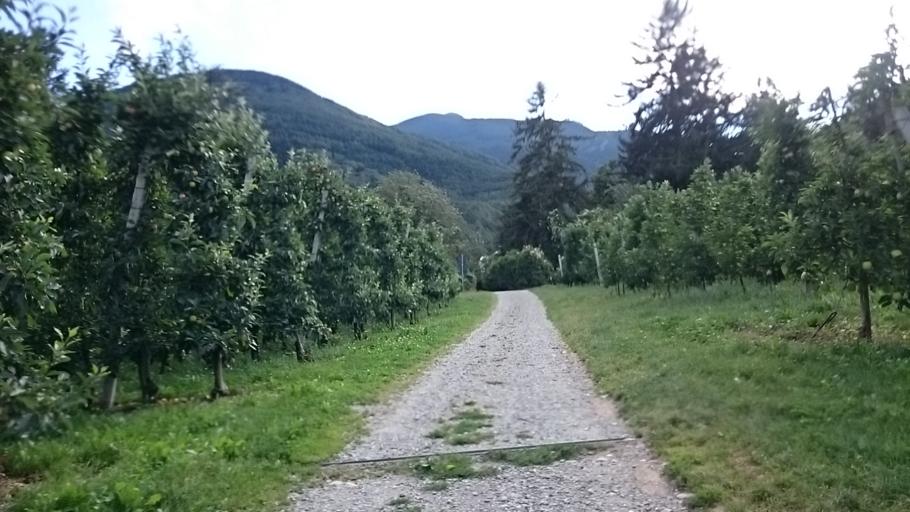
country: IT
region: Trentino-Alto Adige
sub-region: Bolzano
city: Varna
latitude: 46.7438
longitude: 11.6360
